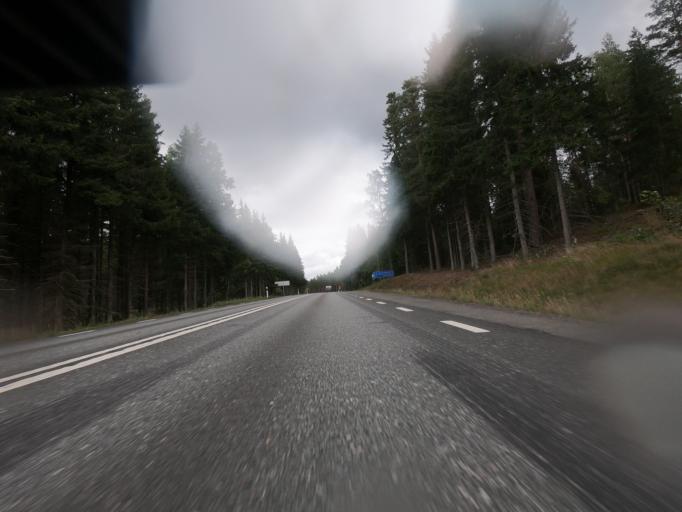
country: SE
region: Joenkoeping
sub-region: Savsjo Kommun
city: Vrigstad
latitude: 57.4408
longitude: 14.3180
